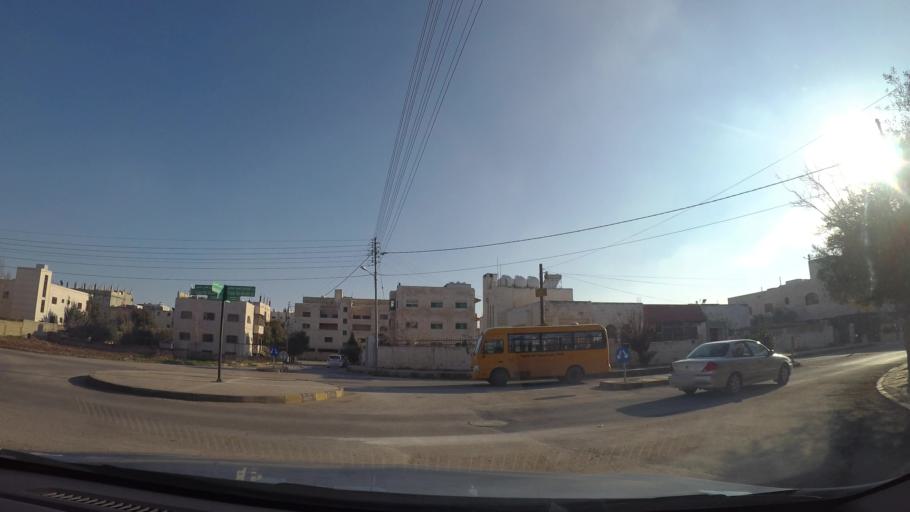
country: JO
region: Amman
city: Al Bunayyat ash Shamaliyah
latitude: 31.8973
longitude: 35.9108
